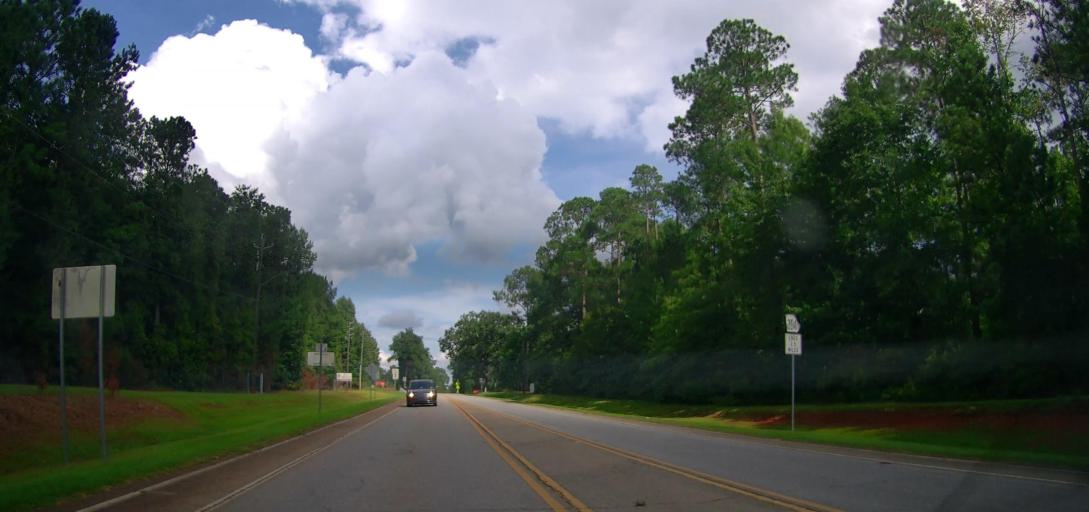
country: US
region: Georgia
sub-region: Harris County
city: Pine Mountain
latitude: 32.8522
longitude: -84.8449
